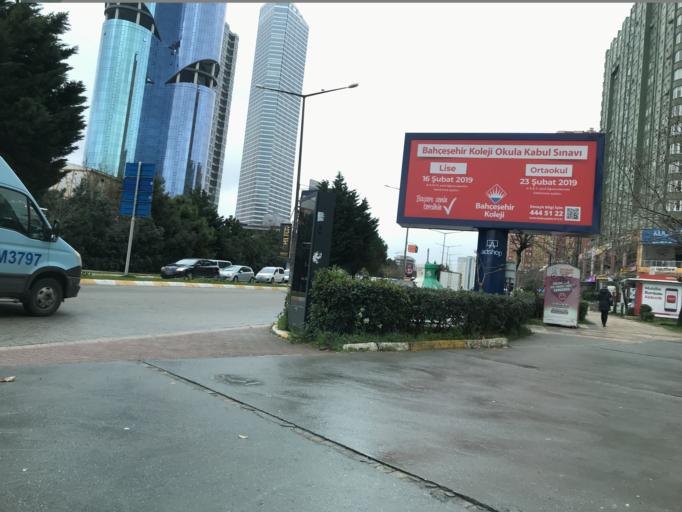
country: TR
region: Istanbul
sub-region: Atasehir
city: Atasehir
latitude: 40.9924
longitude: 29.1161
